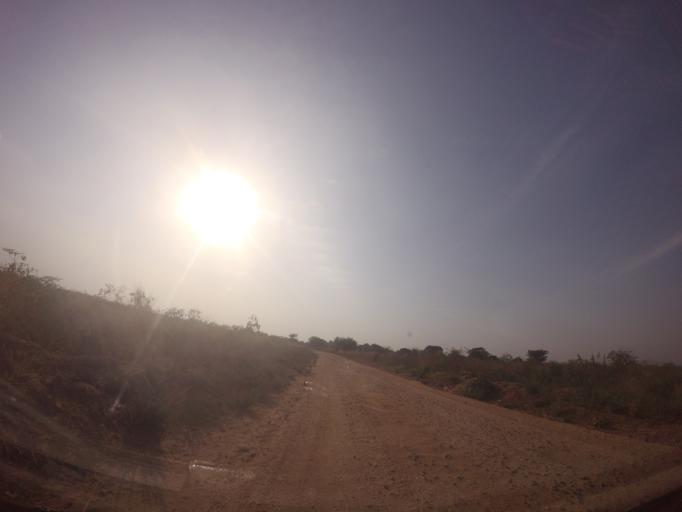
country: UG
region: Northern Region
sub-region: Arua District
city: Arua
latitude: 3.1005
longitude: 31.0950
